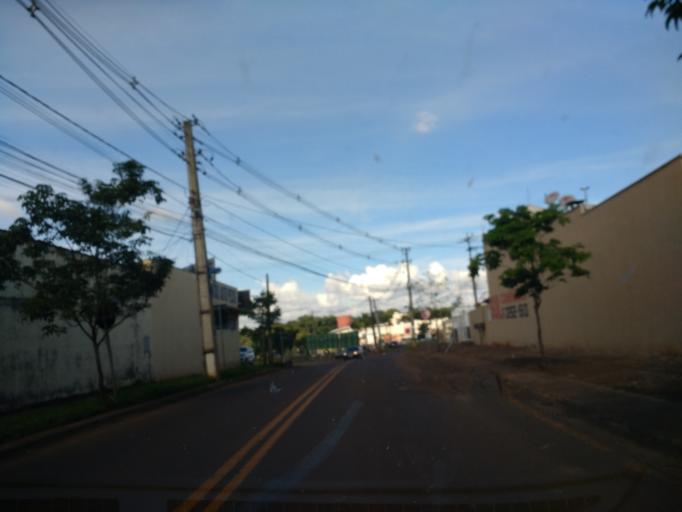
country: BR
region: Parana
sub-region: Maringa
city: Maringa
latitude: -23.4179
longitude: -51.9724
